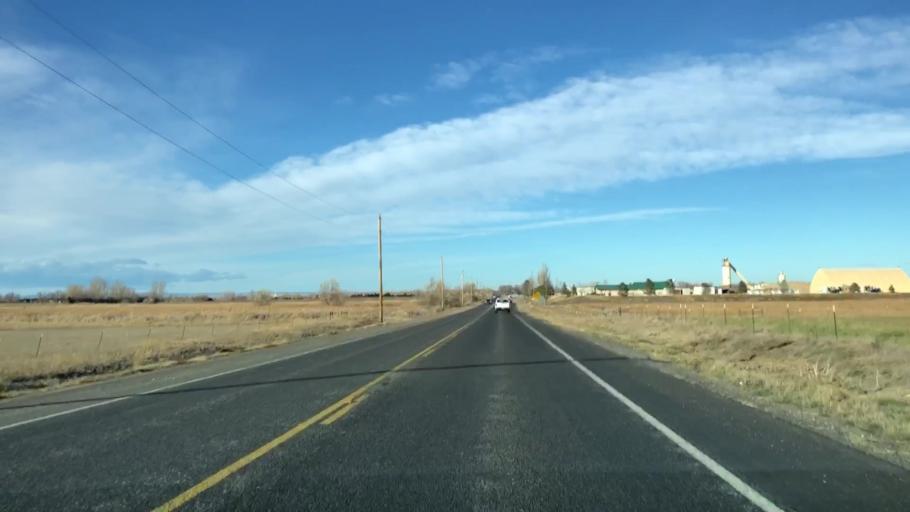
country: US
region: Colorado
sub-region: Weld County
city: Windsor
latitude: 40.4922
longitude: -104.9819
